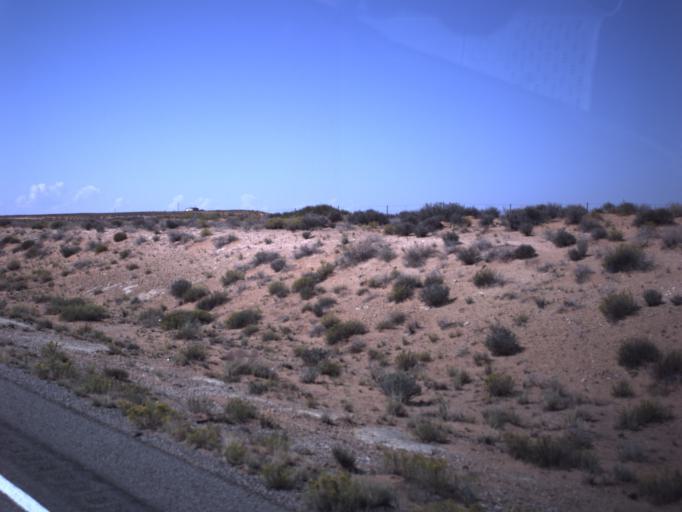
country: US
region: Utah
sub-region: San Juan County
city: Blanding
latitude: 37.0487
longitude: -109.5743
